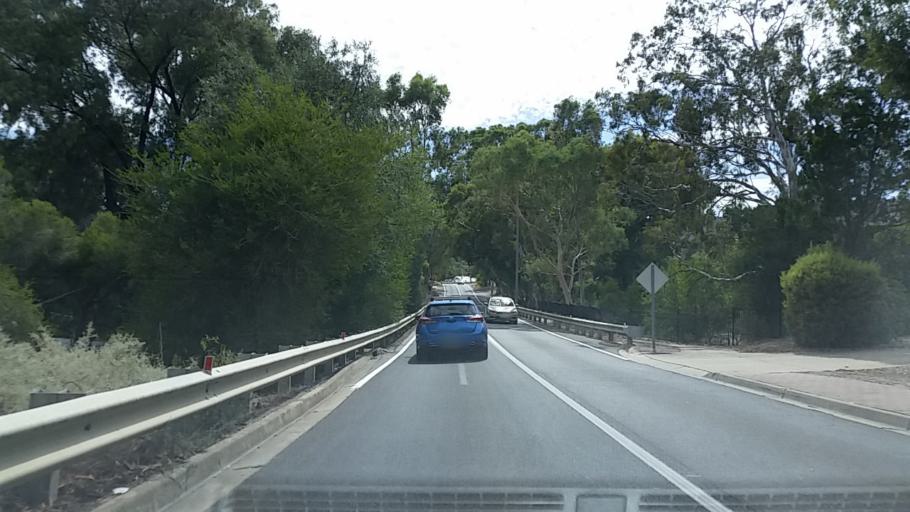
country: AU
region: South Australia
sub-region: Campbelltown
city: Athelstone
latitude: -34.8675
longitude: 138.7079
